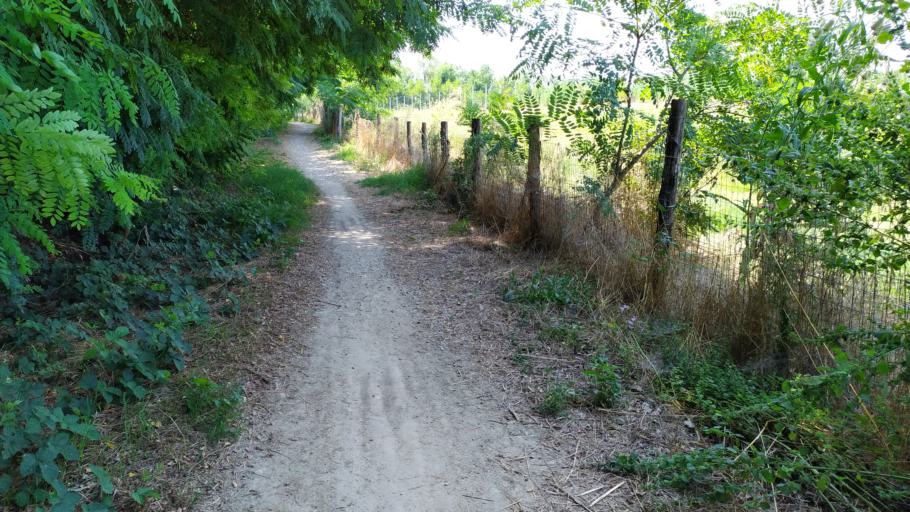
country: IT
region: Emilia-Romagna
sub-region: Forli-Cesena
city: Castrocaro Terme e Terra del Sole
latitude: 44.2012
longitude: 11.9975
